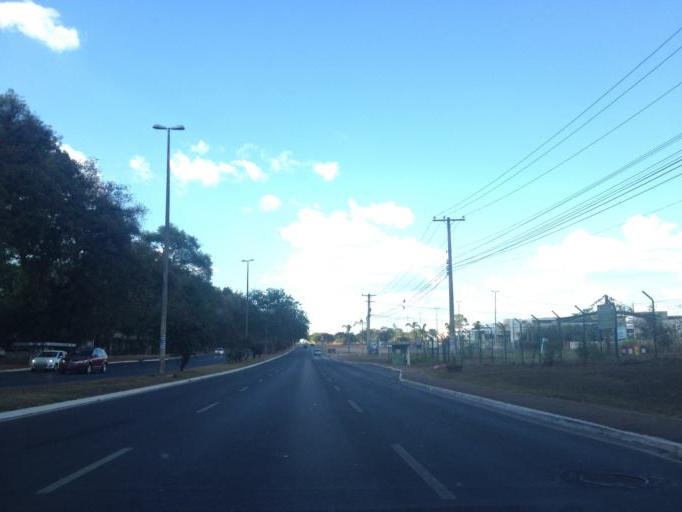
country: BR
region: Federal District
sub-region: Brasilia
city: Brasilia
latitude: -15.8356
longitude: -47.9153
